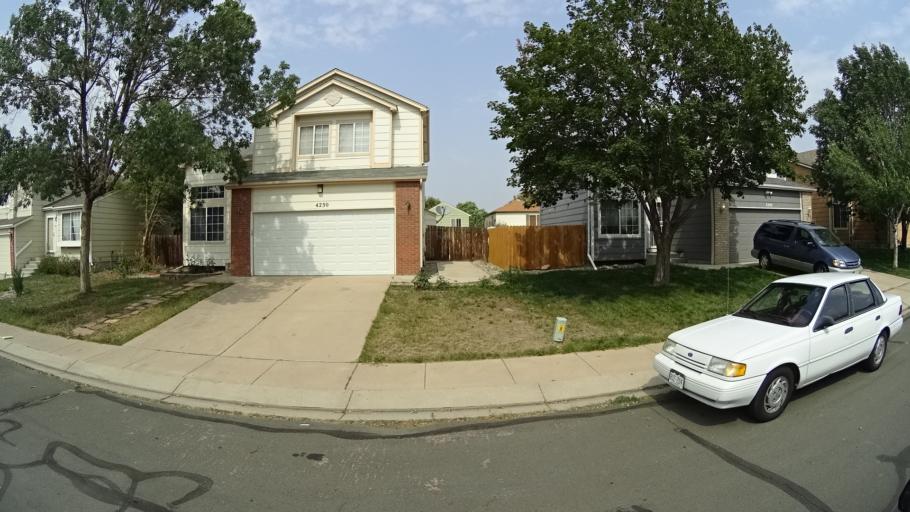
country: US
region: Colorado
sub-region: El Paso County
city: Cimarron Hills
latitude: 38.8236
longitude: -104.7463
